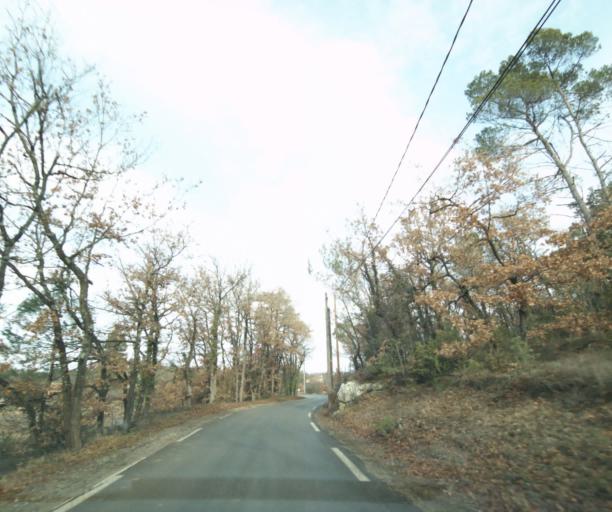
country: FR
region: Provence-Alpes-Cote d'Azur
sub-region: Departement du Var
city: Rougiers
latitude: 43.4069
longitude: 5.8770
